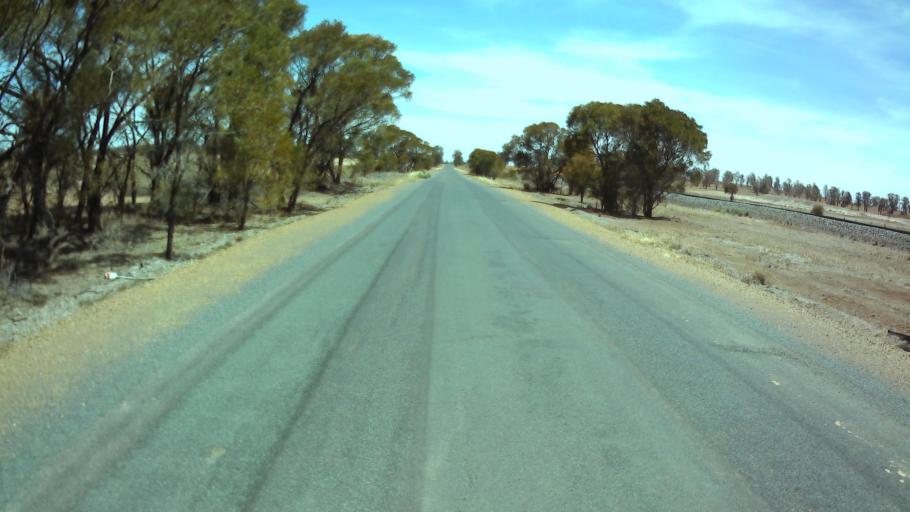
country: AU
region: New South Wales
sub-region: Weddin
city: Grenfell
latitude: -33.7642
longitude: 147.7597
